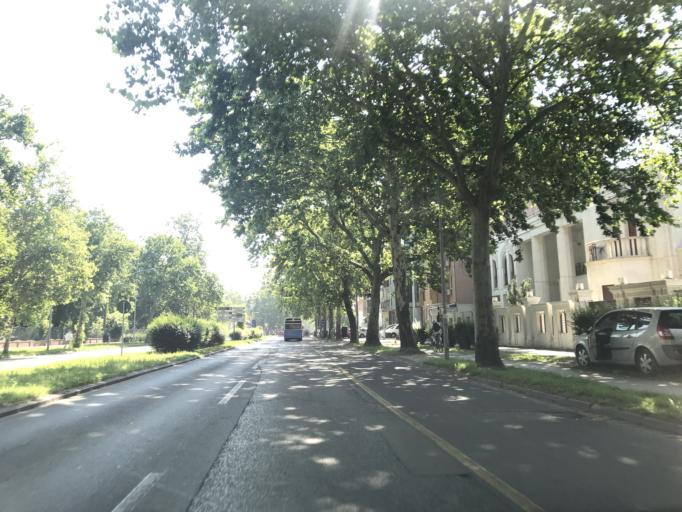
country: RS
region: Autonomna Pokrajina Vojvodina
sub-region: Juznobacki Okrug
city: Novi Sad
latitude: 45.2493
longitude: 19.8219
